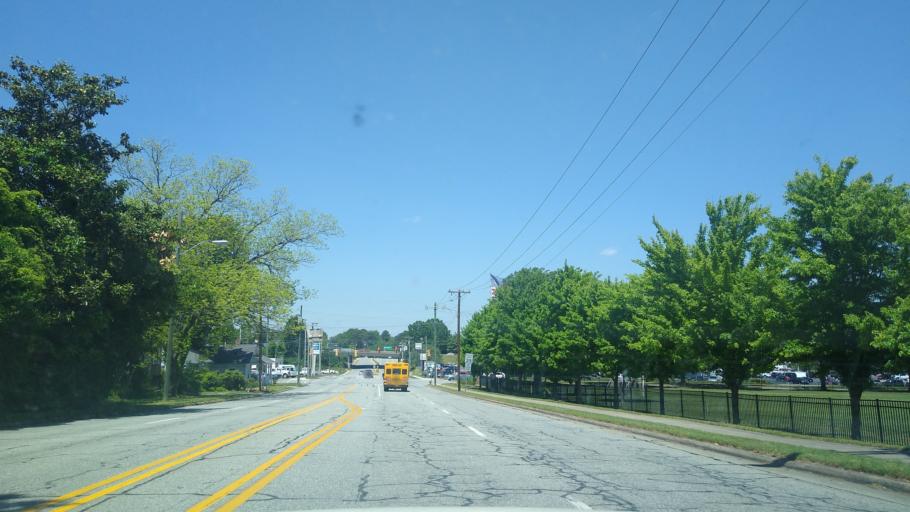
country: US
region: North Carolina
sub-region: Guilford County
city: Greensboro
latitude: 36.0845
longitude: -79.7828
